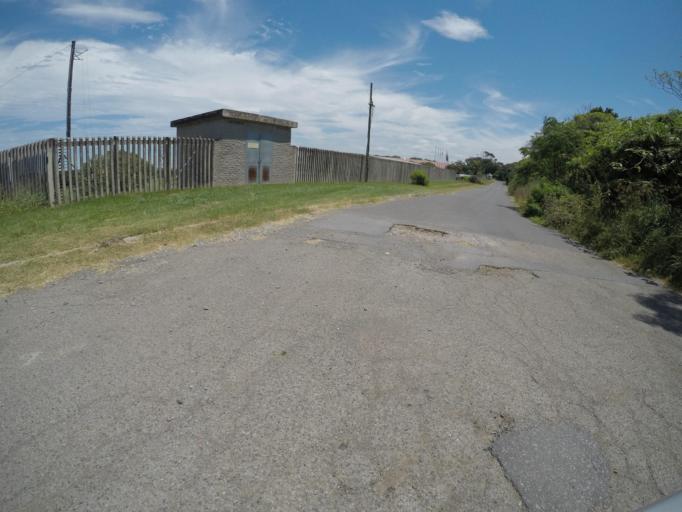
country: ZA
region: Eastern Cape
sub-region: Buffalo City Metropolitan Municipality
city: East London
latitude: -33.0365
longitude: 27.8455
